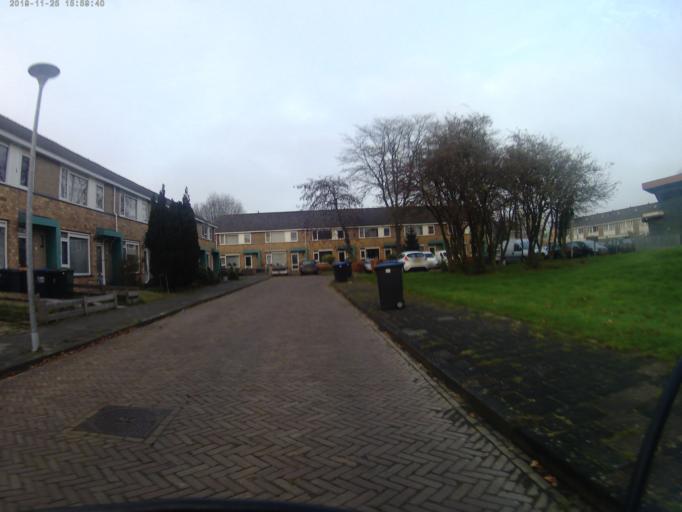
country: NL
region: Drenthe
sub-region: Gemeente Assen
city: Assen
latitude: 53.0083
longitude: 6.5622
